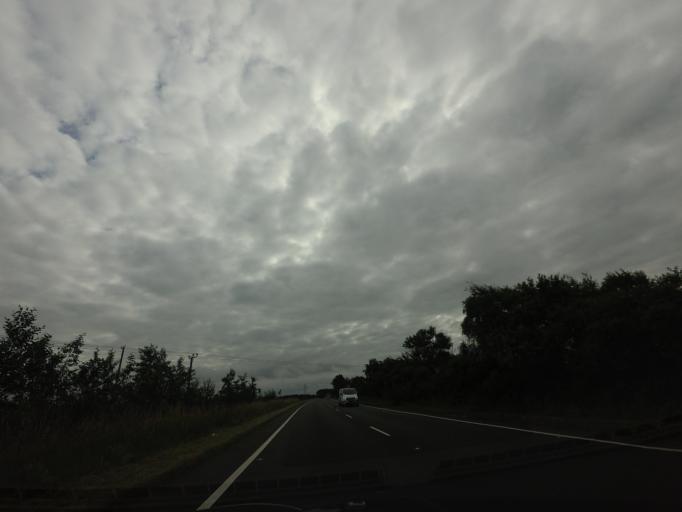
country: GB
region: Scotland
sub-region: Dumfries and Galloway
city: Annan
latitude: 54.9921
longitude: -3.1679
